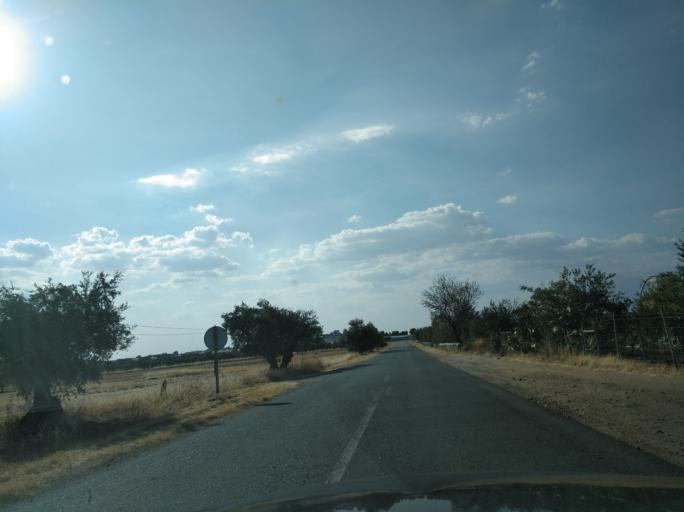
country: PT
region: Evora
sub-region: Mourao
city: Mourao
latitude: 38.3768
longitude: -7.3274
